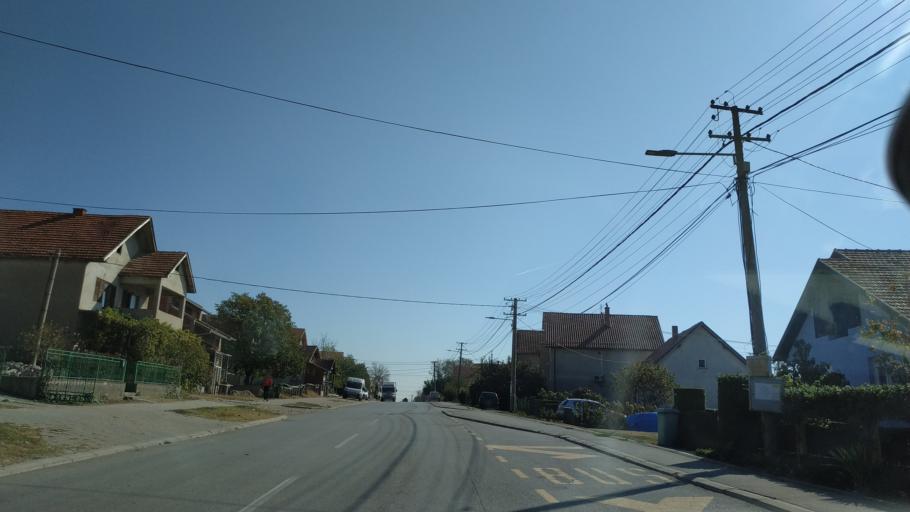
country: RS
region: Central Serbia
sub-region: Nisavski Okrug
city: Aleksinac
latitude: 43.5458
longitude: 21.6955
